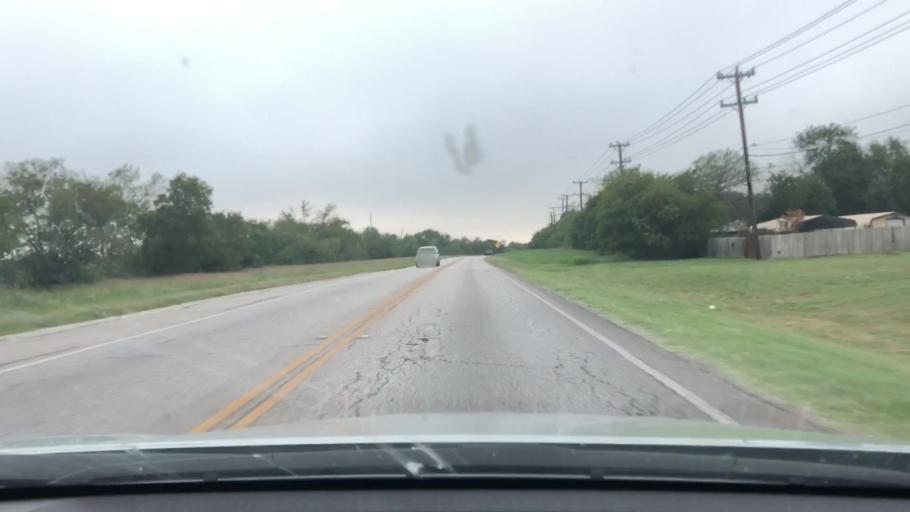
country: US
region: Texas
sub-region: Bexar County
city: Converse
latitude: 29.5036
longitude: -98.3416
